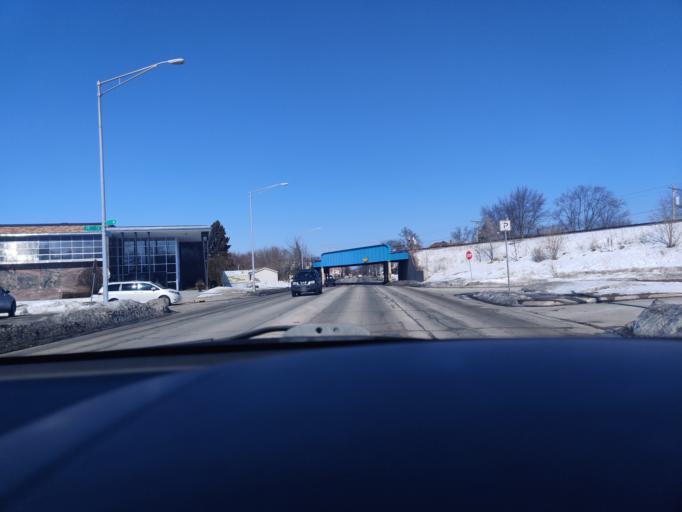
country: US
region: Wisconsin
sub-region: Kenosha County
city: Kenosha
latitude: 42.5676
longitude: -87.8248
